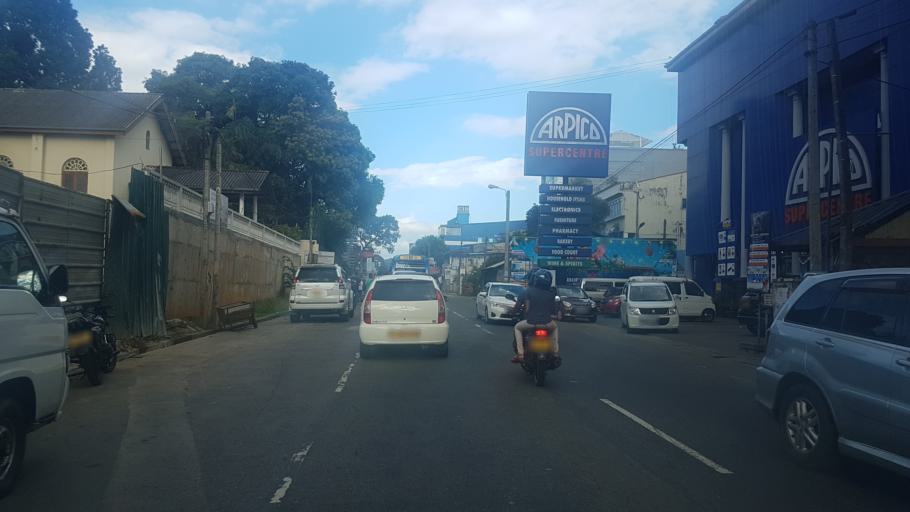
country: LK
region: Central
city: Kandy
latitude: 7.2806
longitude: 80.6197
